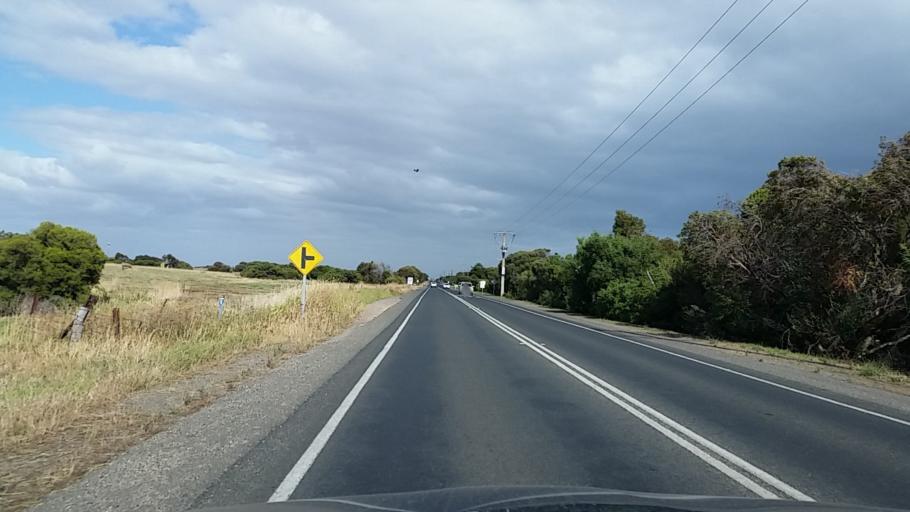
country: AU
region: South Australia
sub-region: Alexandrina
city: Port Elliot
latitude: -35.5077
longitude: 138.7118
